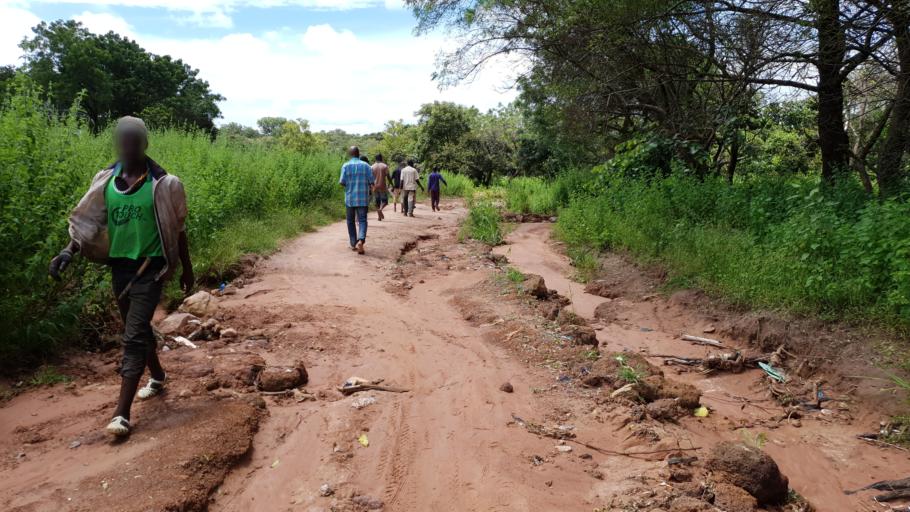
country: CI
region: Savanes
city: Tengrela
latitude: 10.3567
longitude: -6.9183
